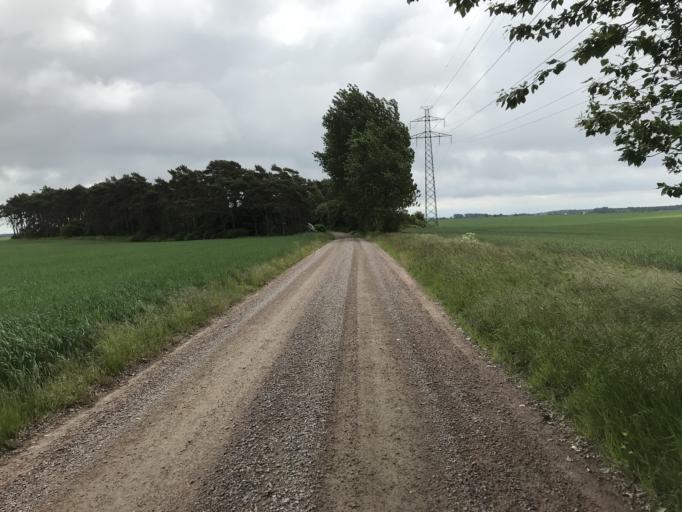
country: SE
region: Skane
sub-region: Landskrona
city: Asmundtorp
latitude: 55.8721
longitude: 12.9004
